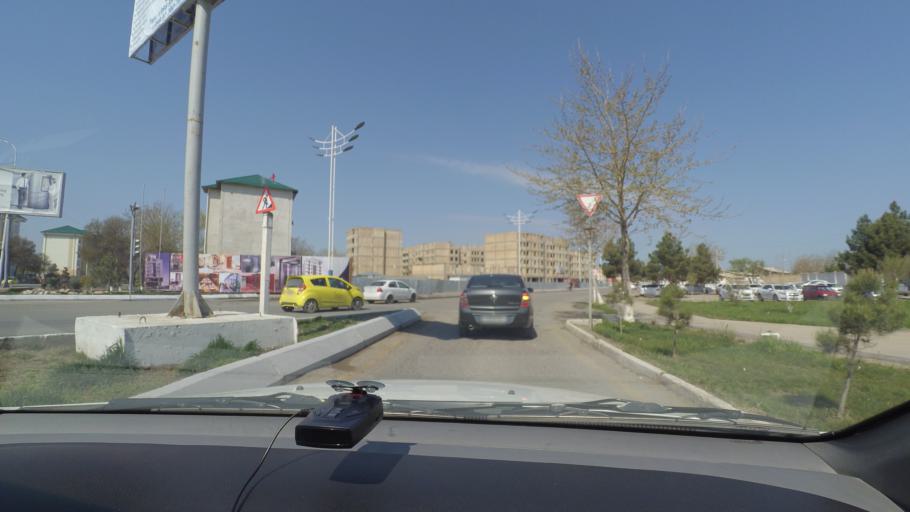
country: UZ
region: Bukhara
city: Bukhara
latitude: 39.7701
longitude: 64.4505
